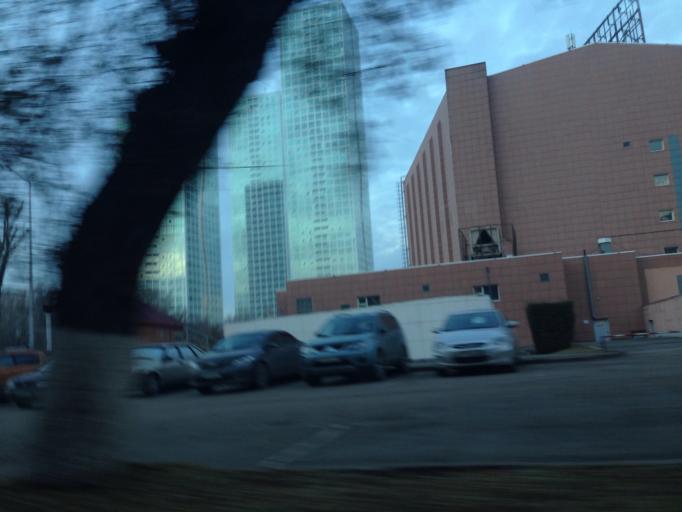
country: KZ
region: Astana Qalasy
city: Astana
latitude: 51.1637
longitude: 71.4235
